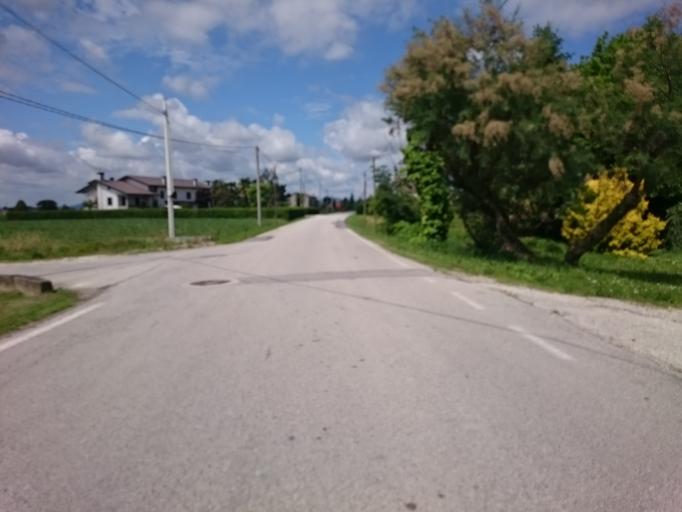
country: IT
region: Veneto
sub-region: Provincia di Padova
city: Arlesega
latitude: 45.4613
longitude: 11.7334
